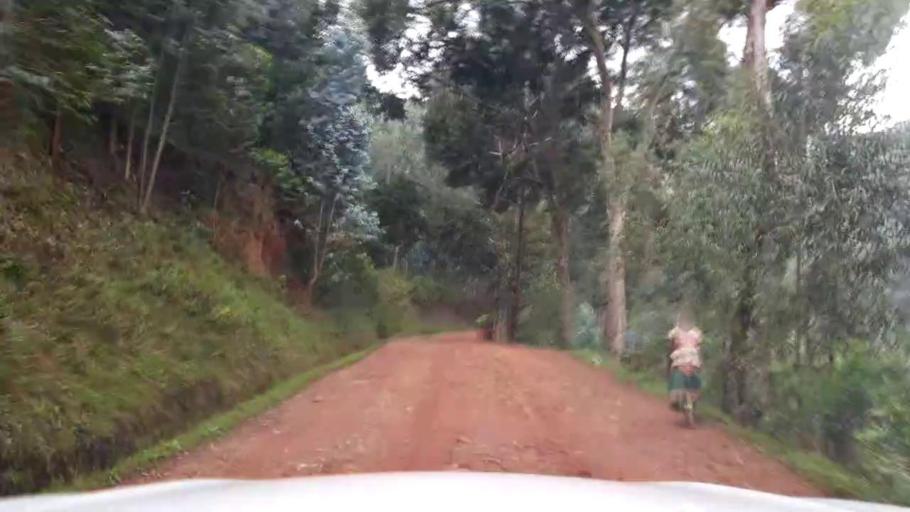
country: UG
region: Western Region
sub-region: Kisoro District
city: Kisoro
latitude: -1.3959
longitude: 29.8011
